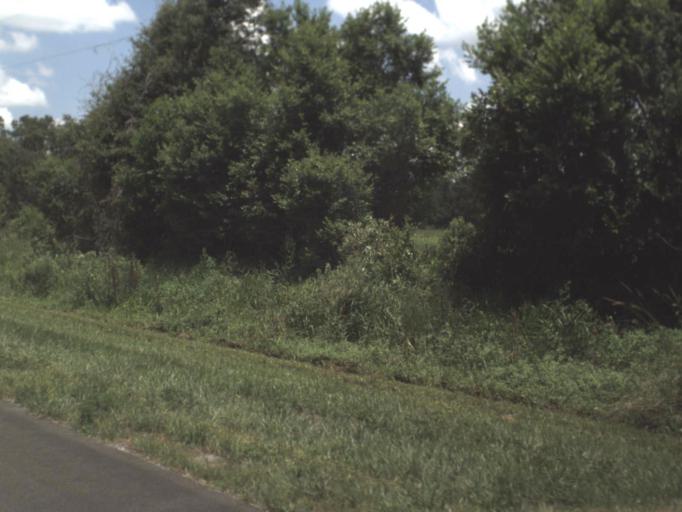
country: US
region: Florida
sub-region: Alachua County
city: Alachua
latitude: 29.8296
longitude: -82.3962
